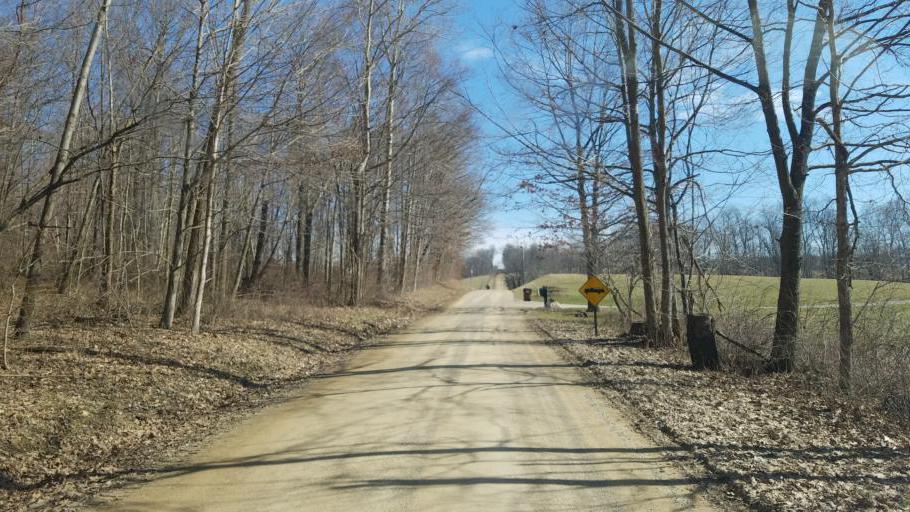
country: US
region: Ohio
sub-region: Knox County
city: Fredericktown
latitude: 40.5090
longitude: -82.4143
